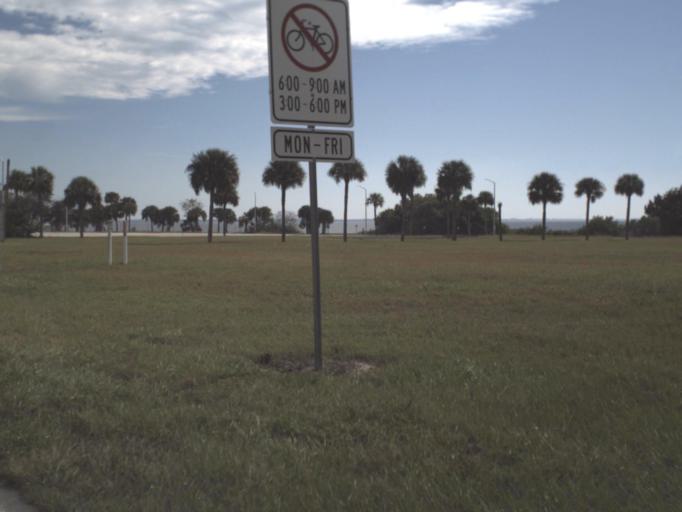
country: US
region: Florida
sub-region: Brevard County
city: Port Saint John
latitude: 28.5276
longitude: -80.7808
